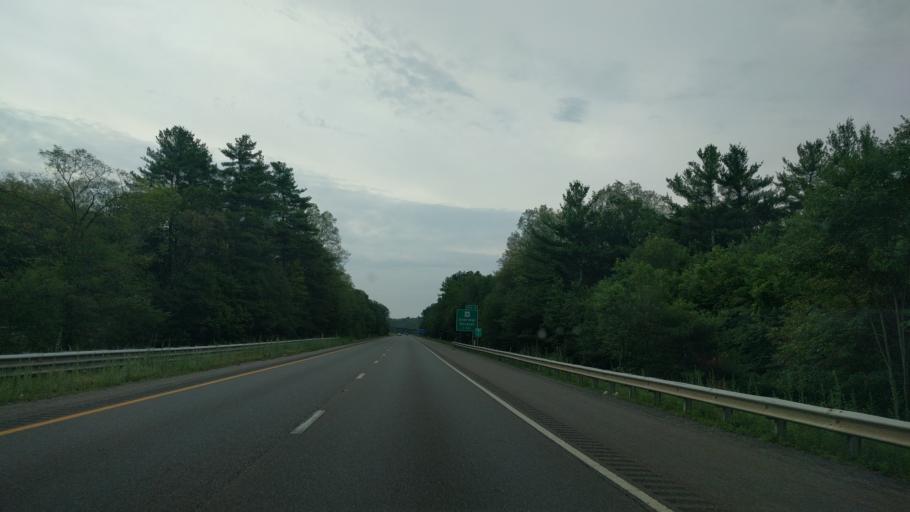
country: US
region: Massachusetts
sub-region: Worcester County
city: East Douglas
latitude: 42.0820
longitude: -71.6893
